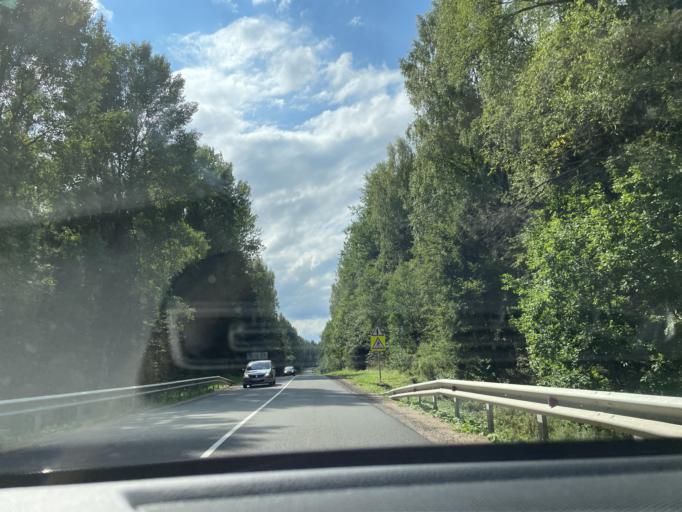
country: RU
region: Novgorod
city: Valday
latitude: 58.0345
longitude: 33.2196
